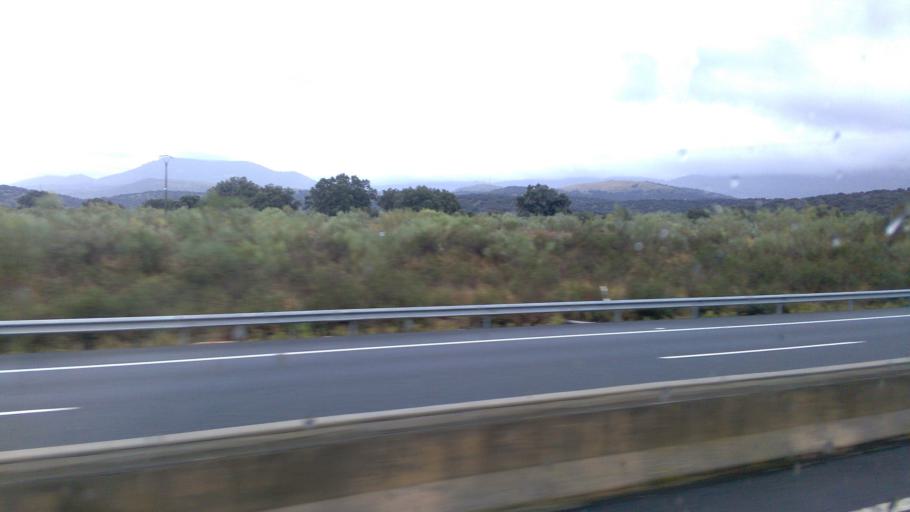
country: ES
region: Extremadura
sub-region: Provincia de Caceres
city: Romangordo
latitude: 39.7834
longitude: -5.7281
